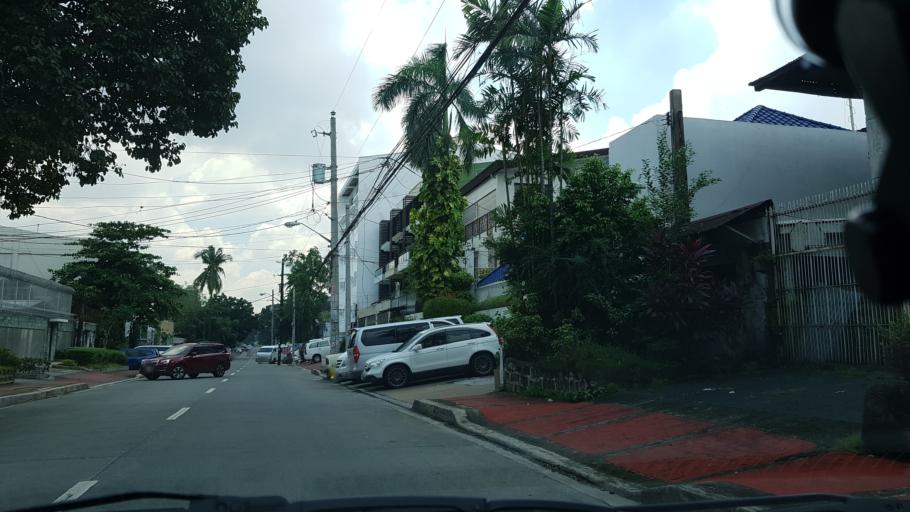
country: PH
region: Calabarzon
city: Del Monte
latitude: 14.6325
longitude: 121.0261
